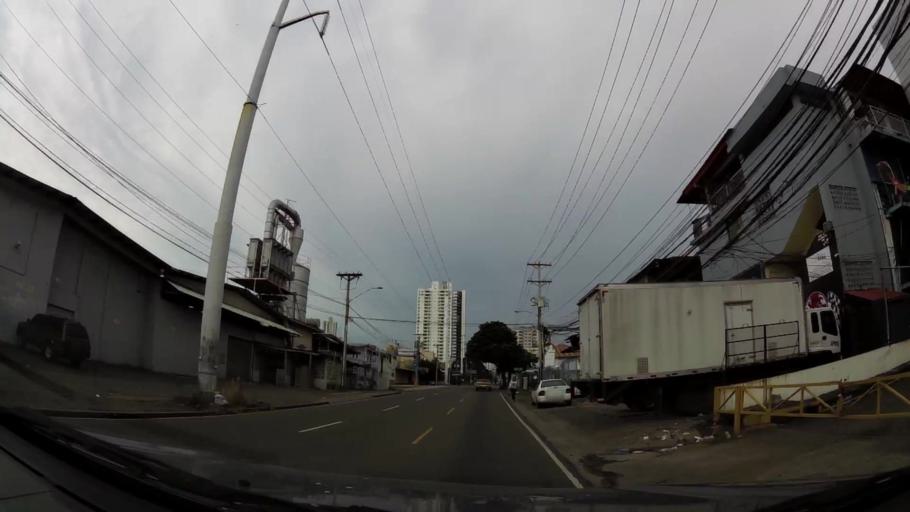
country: PA
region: Panama
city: Panama
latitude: 9.0053
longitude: -79.4966
